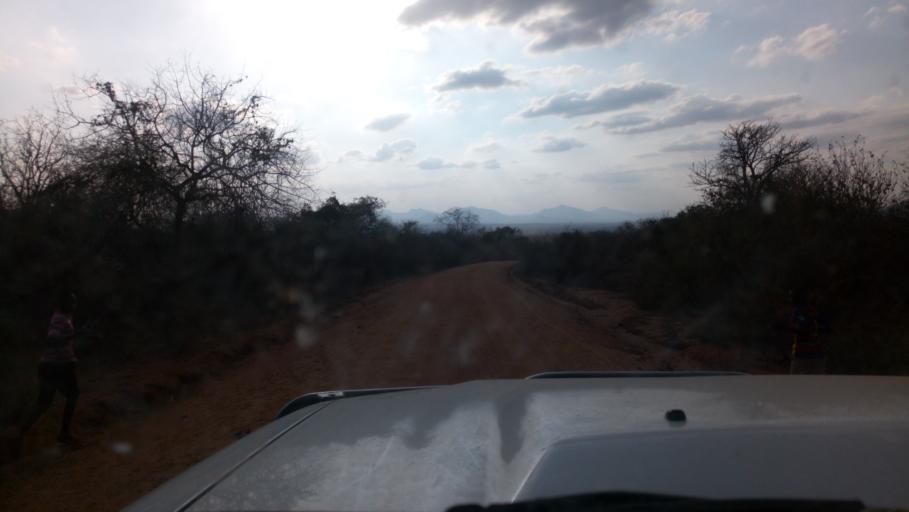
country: KE
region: Kitui
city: Kitui
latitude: -1.6953
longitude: 38.3579
